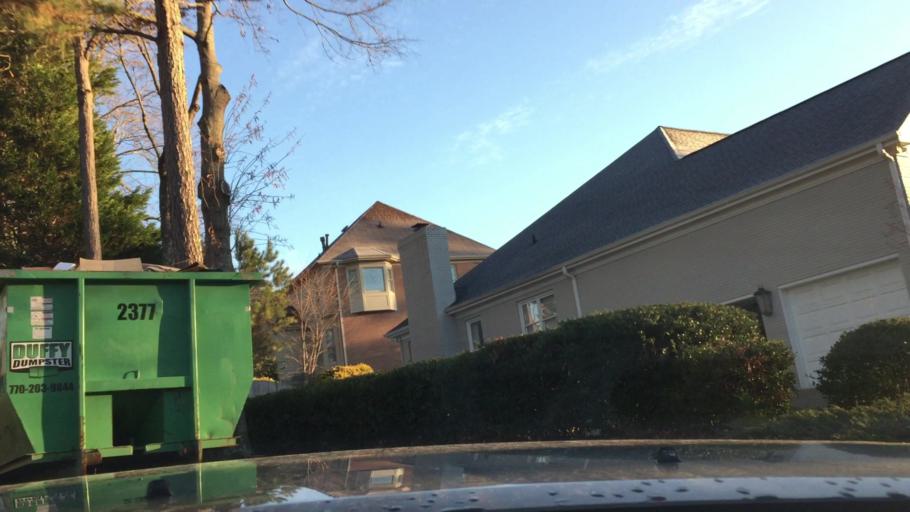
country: US
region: Georgia
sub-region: Forsyth County
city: Cumming
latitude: 34.1872
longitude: -84.2031
